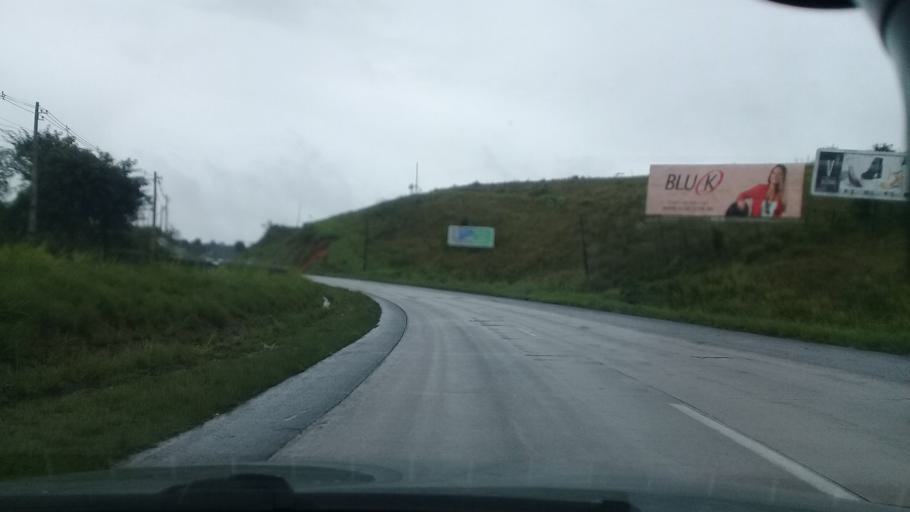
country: BR
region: Pernambuco
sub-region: Jaboatao Dos Guararapes
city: Jaboatao dos Guararapes
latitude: -8.0937
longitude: -35.0319
